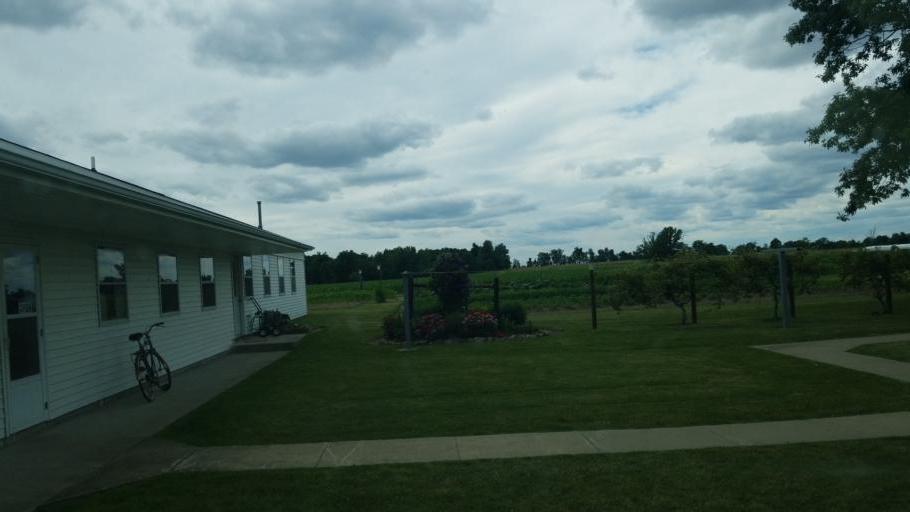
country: US
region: Michigan
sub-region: Barry County
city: Nashville
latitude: 42.6775
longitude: -84.9761
